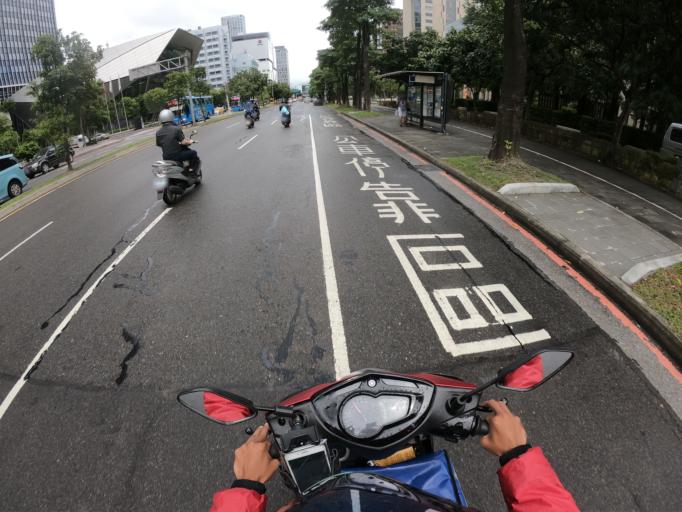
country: TW
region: Taipei
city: Taipei
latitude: 25.0335
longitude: 121.5684
